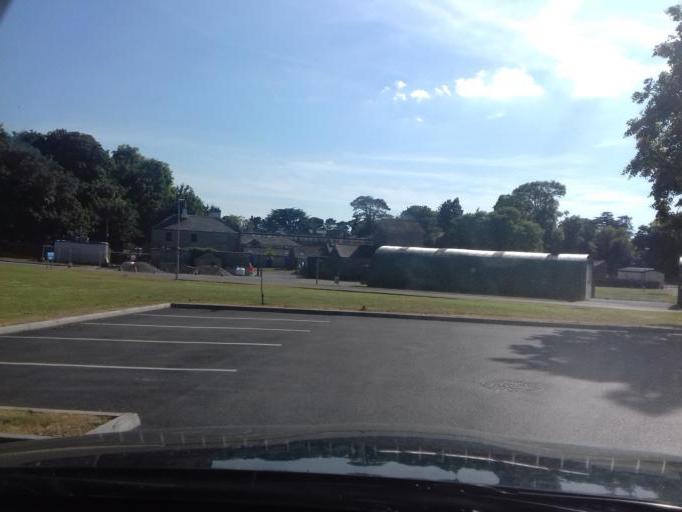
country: IE
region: Leinster
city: Castleknock
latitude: 53.3942
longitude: -6.3554
